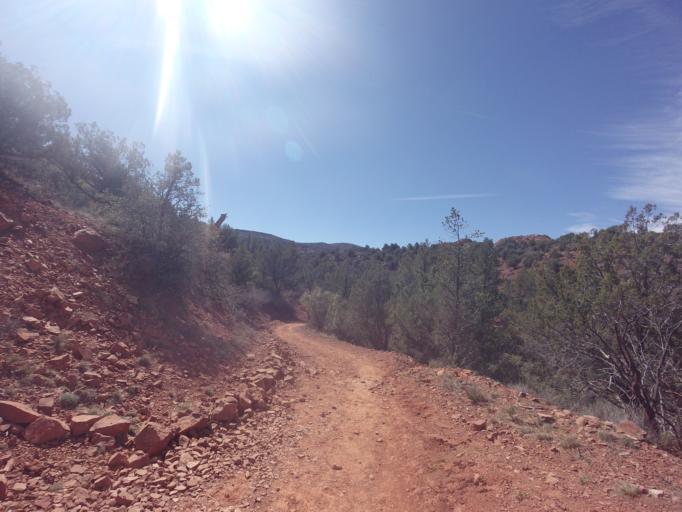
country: US
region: Arizona
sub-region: Yavapai County
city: West Sedona
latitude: 34.8092
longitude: -111.8233
